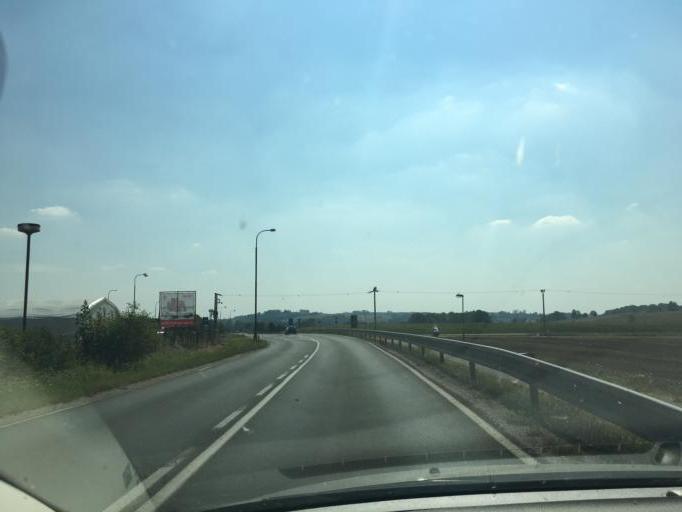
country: CZ
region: Kralovehradecky
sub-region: Okres Trutnov
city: Vrchlabi
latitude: 50.6227
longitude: 15.6448
